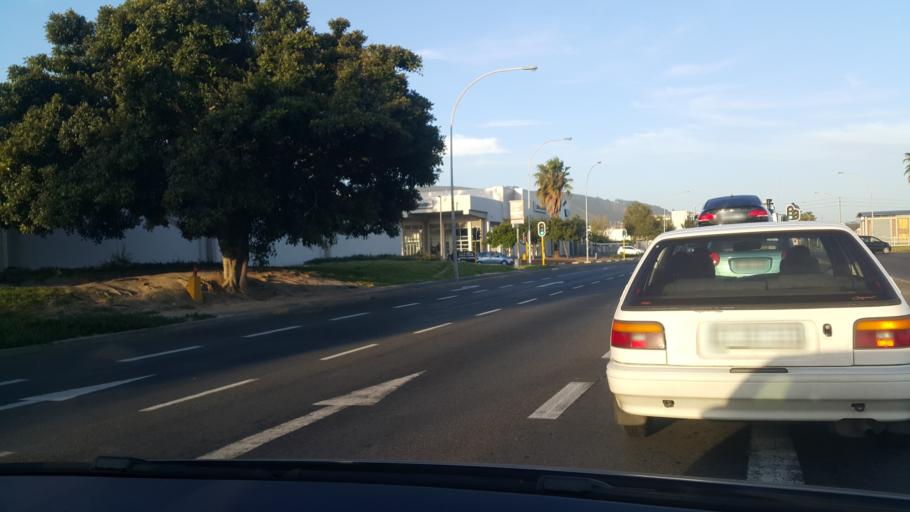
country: ZA
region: Western Cape
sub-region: City of Cape Town
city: Sunset Beach
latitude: -33.8943
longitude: 18.5629
